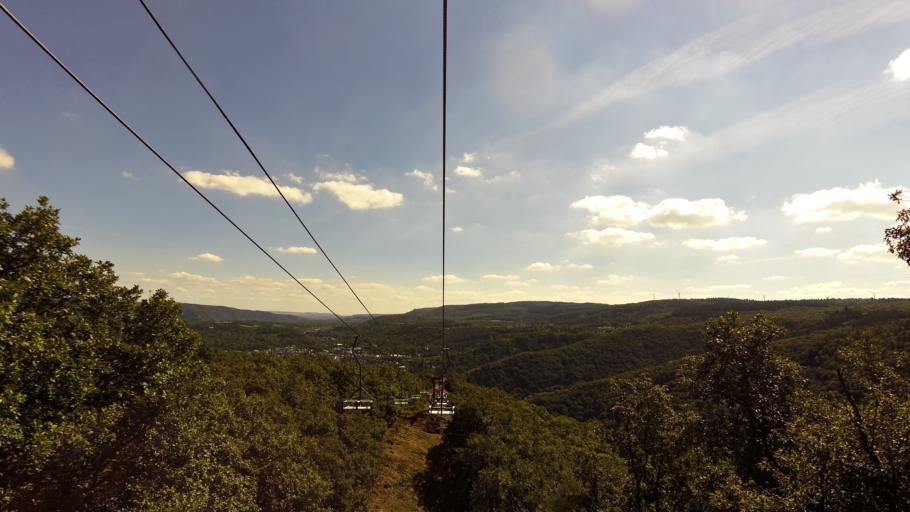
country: DE
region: Rheinland-Pfalz
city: Filsen
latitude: 50.2421
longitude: 7.5707
